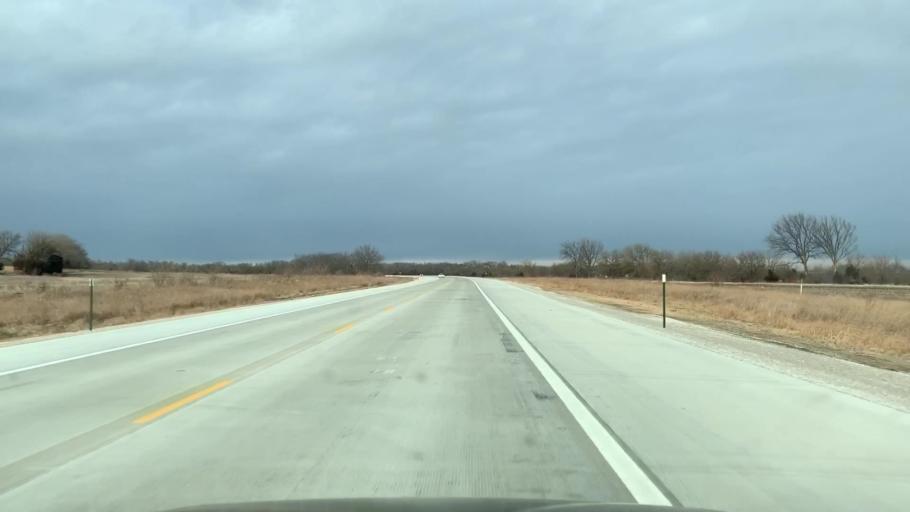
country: US
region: Kansas
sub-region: Allen County
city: Humboldt
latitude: 37.8586
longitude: -95.4065
